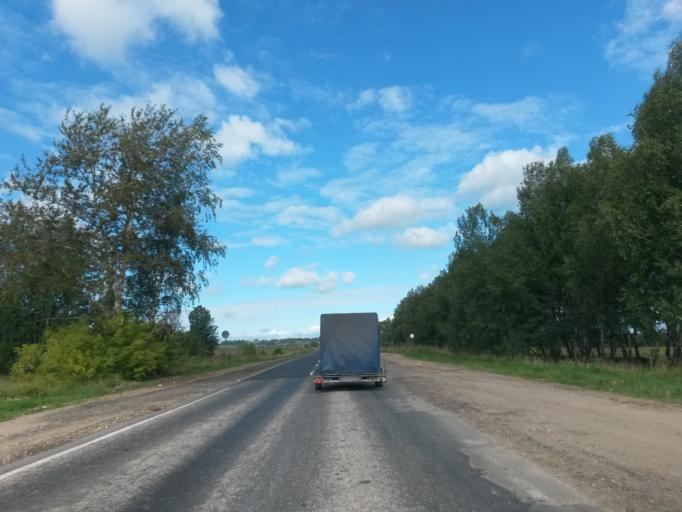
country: RU
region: Jaroslavl
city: Yaroslavl
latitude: 57.5173
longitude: 39.8930
